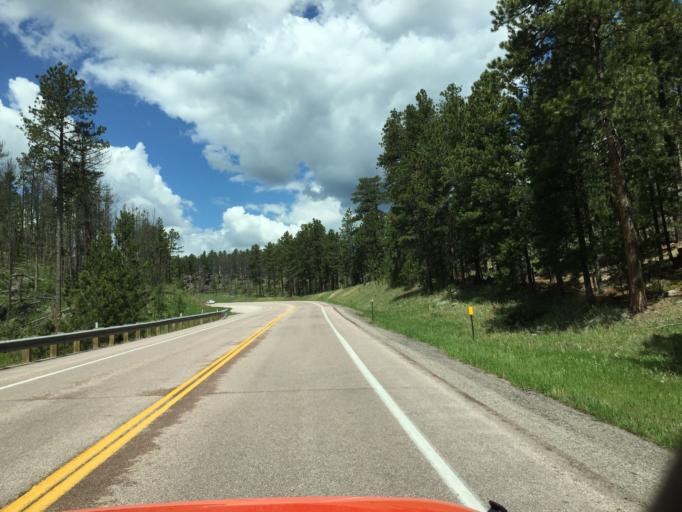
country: US
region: South Dakota
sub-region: Custer County
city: Custer
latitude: 43.8926
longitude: -103.5676
